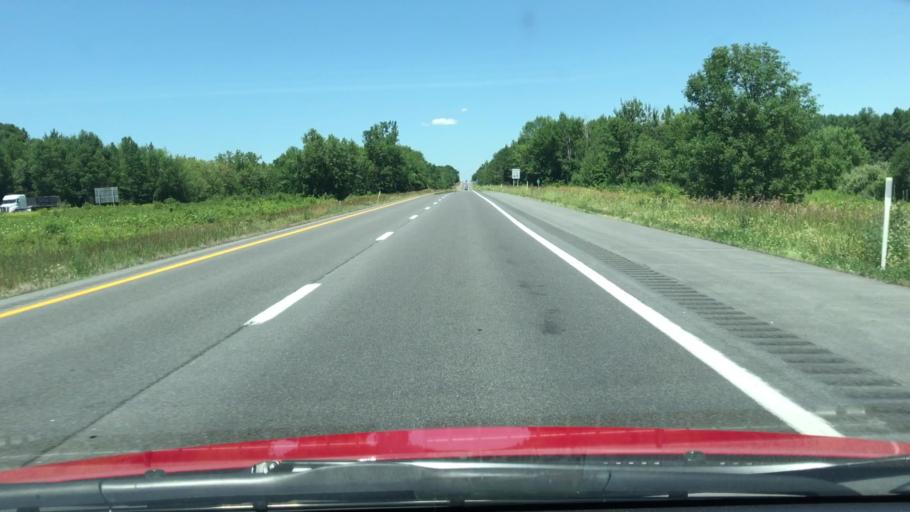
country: US
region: New York
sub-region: Clinton County
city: Cumberland Head
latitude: 44.7914
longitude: -73.4402
